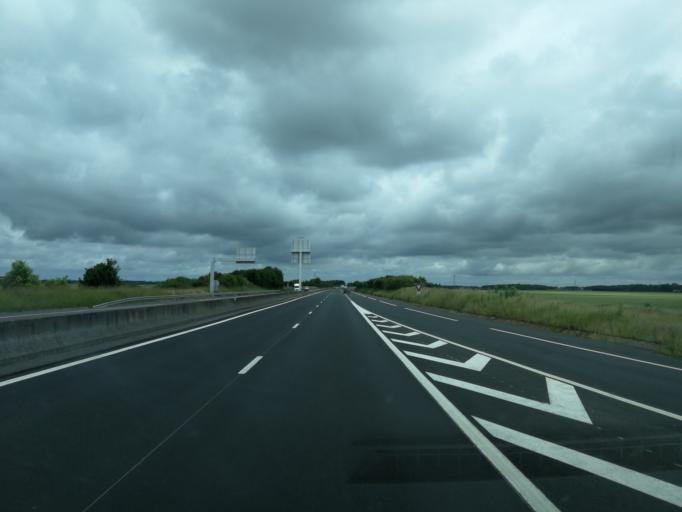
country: FR
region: Haute-Normandie
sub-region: Departement de l'Eure
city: Damville
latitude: 48.8903
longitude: 1.1724
